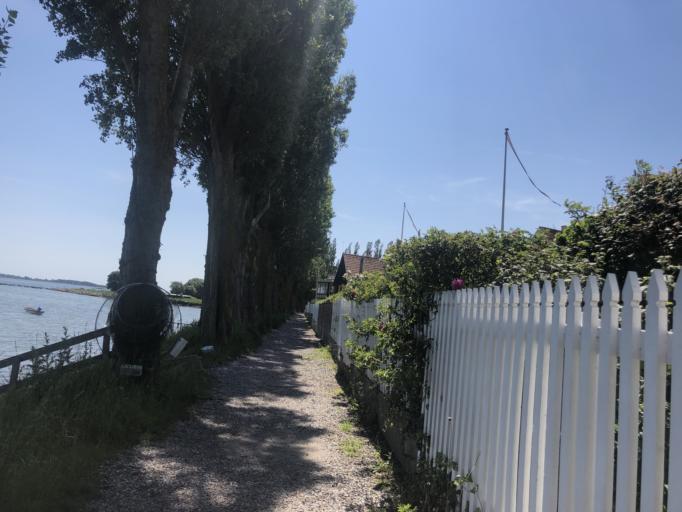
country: DK
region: South Denmark
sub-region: AEro Kommune
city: AEroskobing
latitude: 54.8875
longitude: 10.4141
